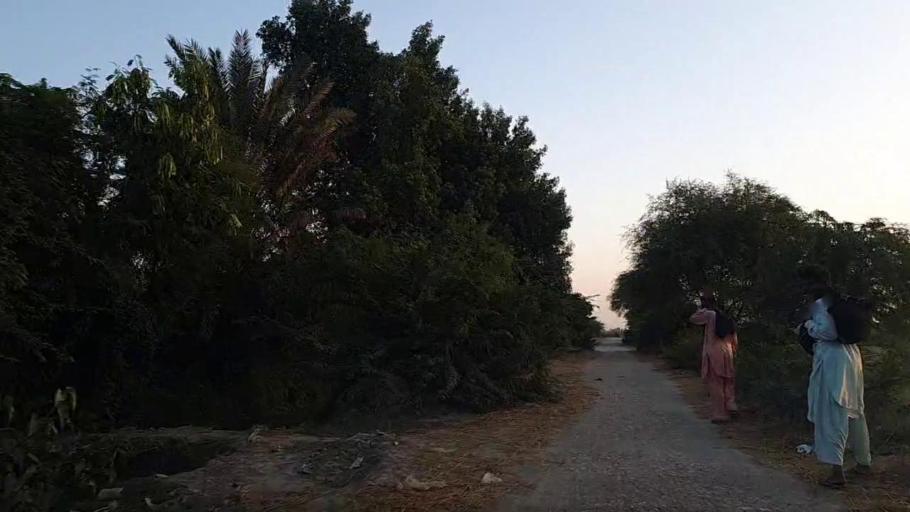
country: PK
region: Sindh
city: Mirpur Batoro
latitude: 24.6420
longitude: 68.1897
